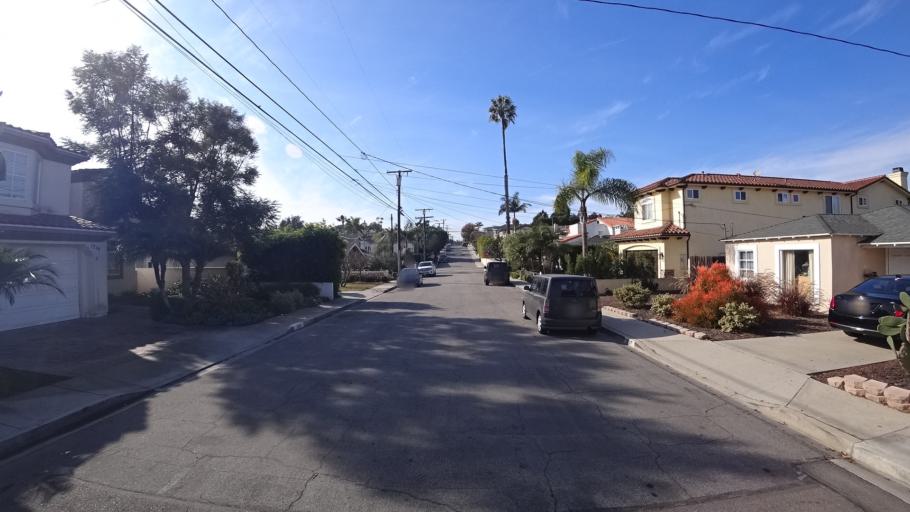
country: US
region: California
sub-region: Los Angeles County
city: Hermosa Beach
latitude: 33.8785
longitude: -118.3822
